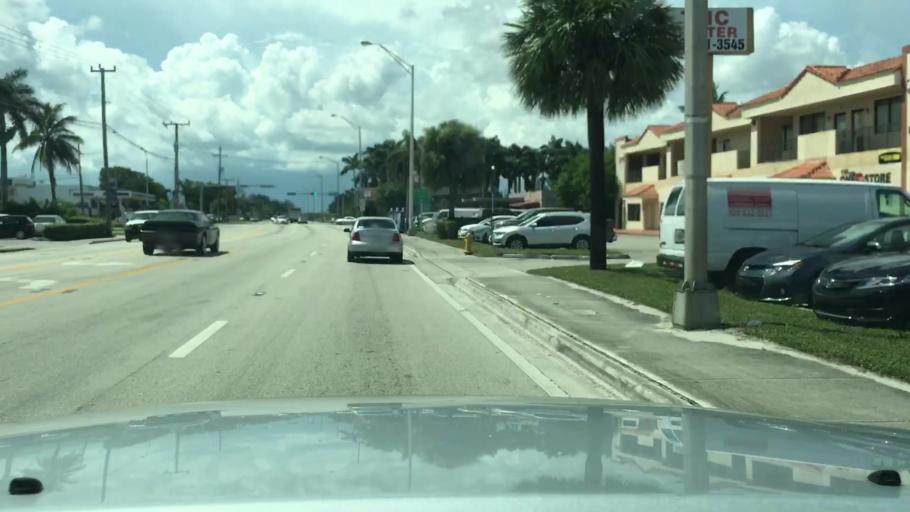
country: US
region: Florida
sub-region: Miami-Dade County
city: Opa-locka
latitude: 25.8966
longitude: -80.2663
